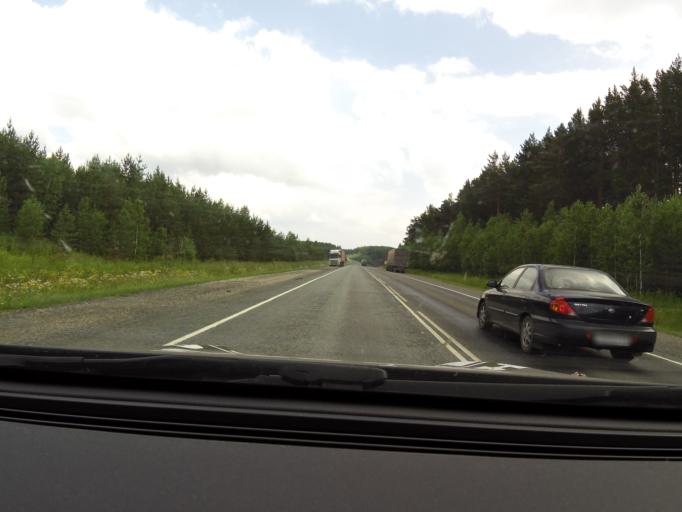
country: RU
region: Sverdlovsk
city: Achit
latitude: 56.7810
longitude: 57.9277
